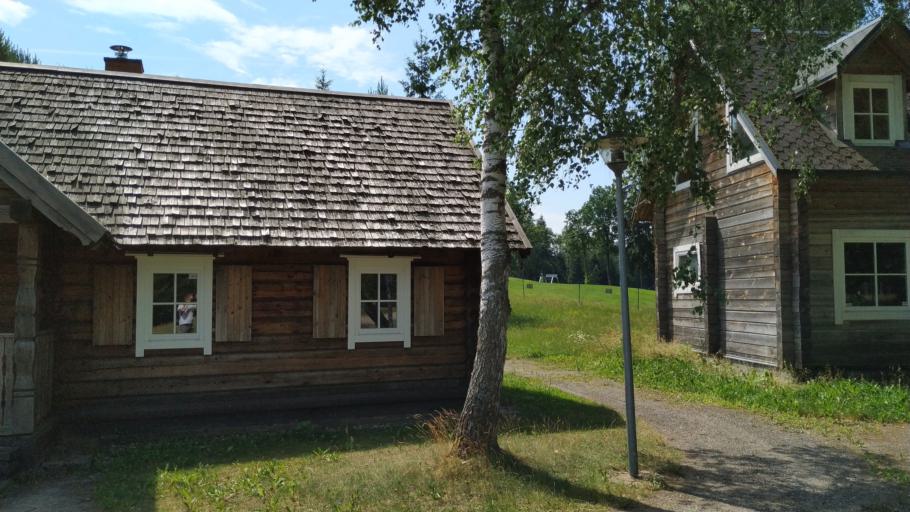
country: LT
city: Nemencine
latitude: 54.9063
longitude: 25.3207
